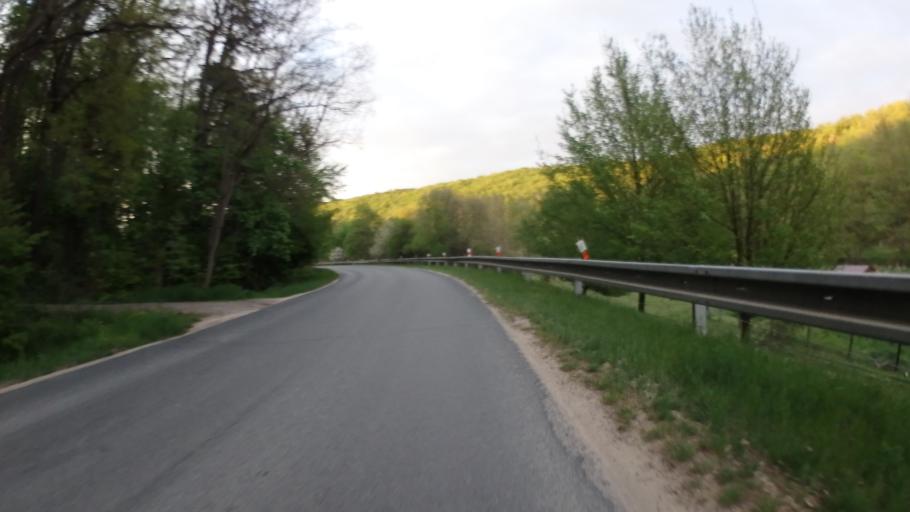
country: CZ
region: South Moravian
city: Strelice
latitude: 49.1443
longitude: 16.4679
